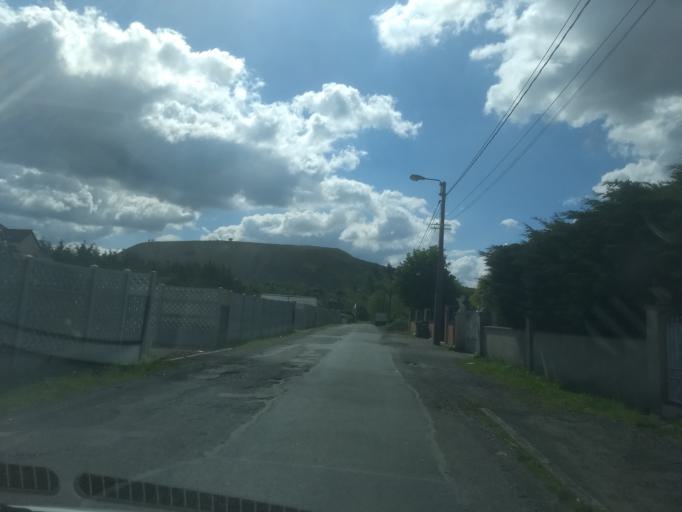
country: FR
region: Nord-Pas-de-Calais
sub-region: Departement du Pas-de-Calais
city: Drocourt
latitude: 50.4090
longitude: 2.9280
